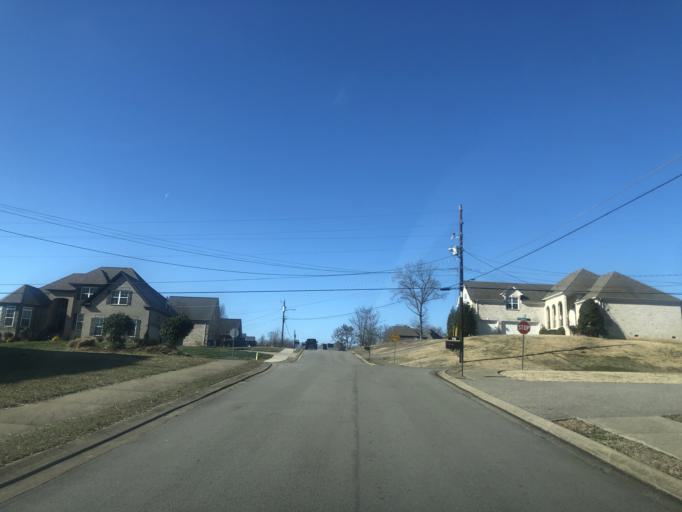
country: US
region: Tennessee
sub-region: Rutherford County
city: Smyrna
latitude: 35.9681
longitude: -86.5407
